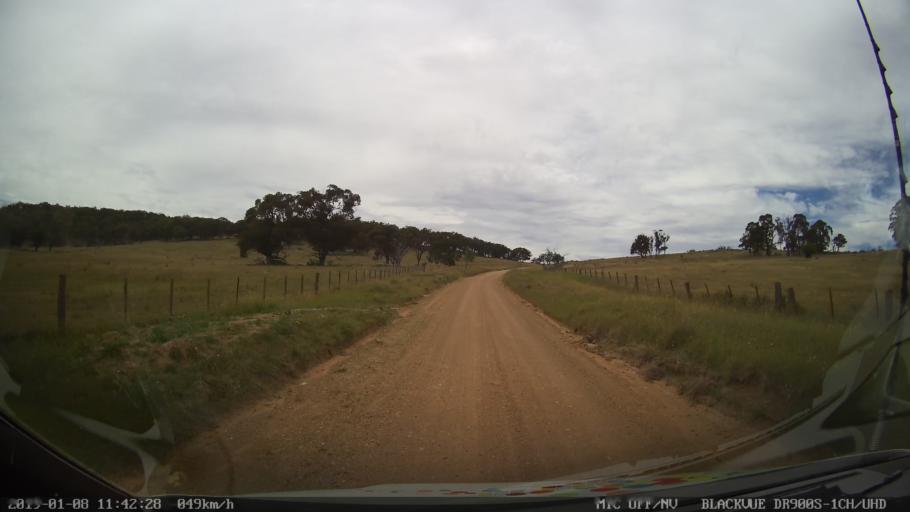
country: AU
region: New South Wales
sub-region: Armidale Dumaresq
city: Armidale
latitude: -30.3784
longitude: 151.5760
